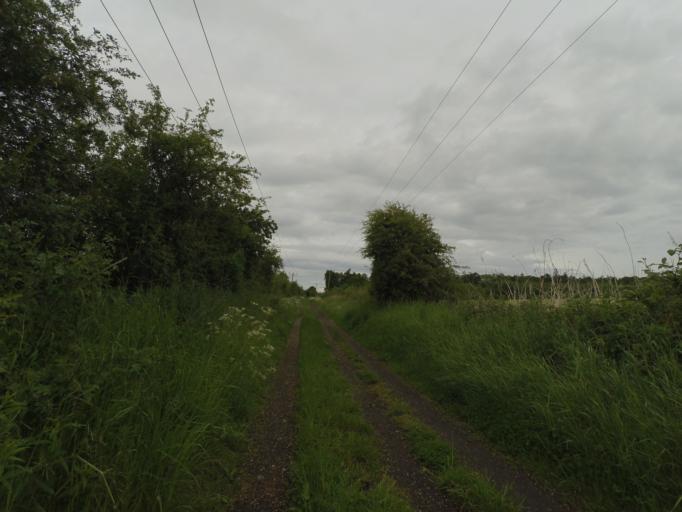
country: GB
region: Scotland
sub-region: East Lothian
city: Macmerry
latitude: 55.9263
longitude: -2.9093
